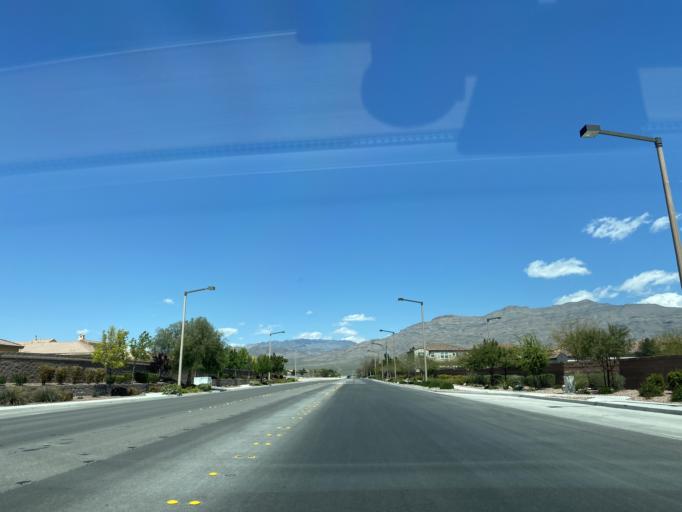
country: US
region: Nevada
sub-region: Clark County
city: North Las Vegas
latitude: 36.3129
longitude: -115.2243
